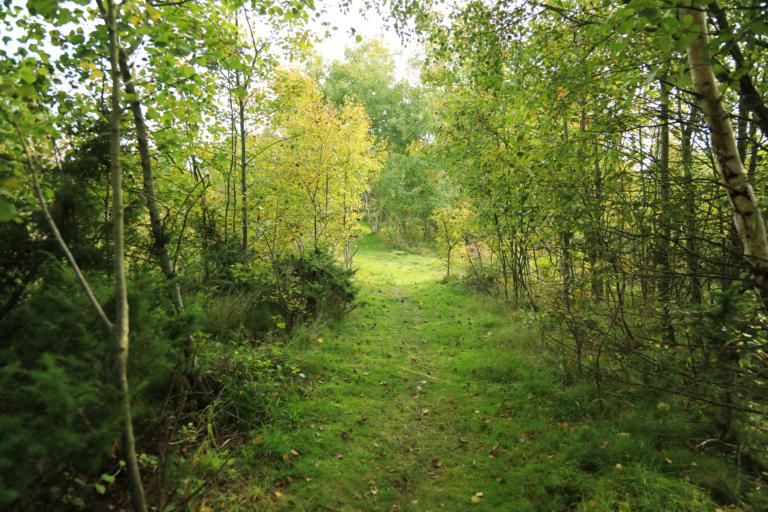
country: SE
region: Halland
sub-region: Varbergs Kommun
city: Varberg
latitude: 57.1192
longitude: 12.2185
